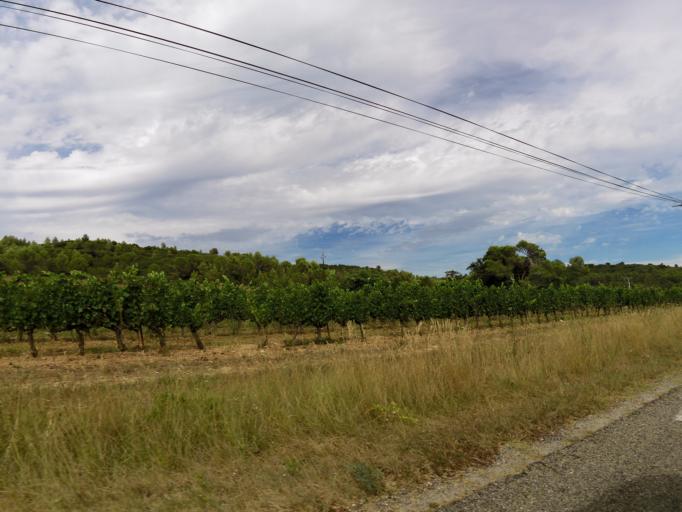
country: FR
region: Languedoc-Roussillon
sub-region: Departement du Gard
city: Congenies
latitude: 43.8023
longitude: 4.1558
